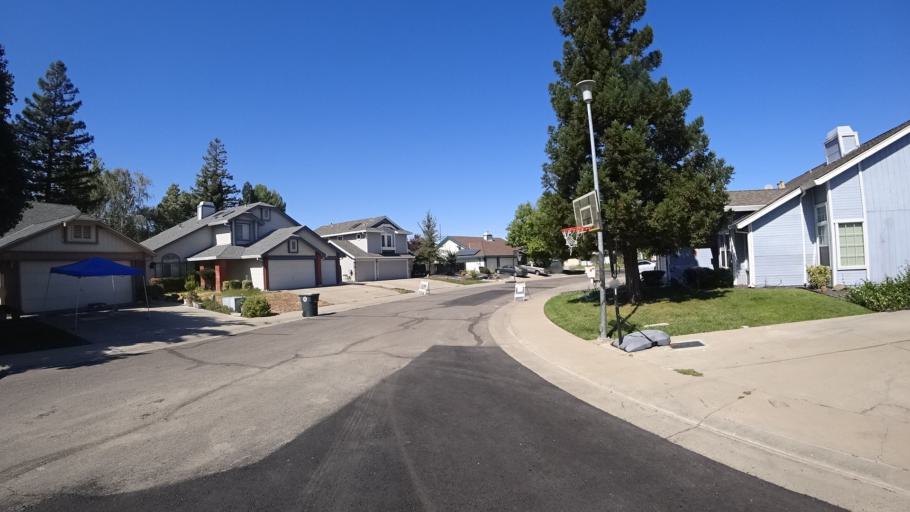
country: US
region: California
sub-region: Sacramento County
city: Laguna
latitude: 38.4290
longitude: -121.4379
